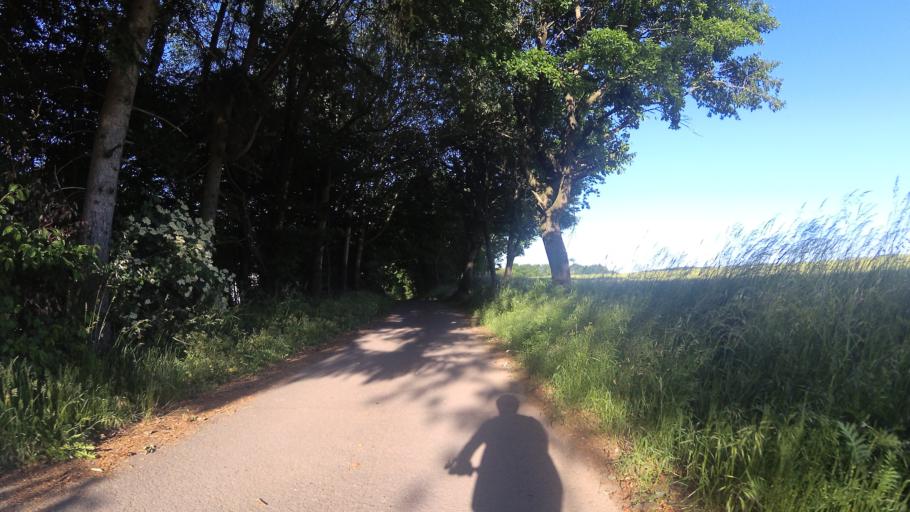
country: DE
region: Saarland
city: Mainzweiler
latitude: 49.4433
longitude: 7.1118
